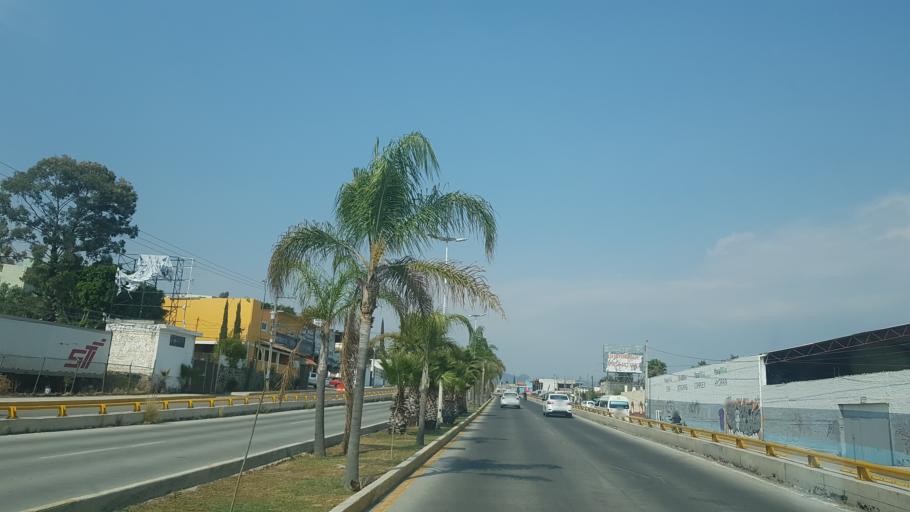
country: MX
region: Puebla
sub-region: Atlixco
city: El Encanto del Cerril
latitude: 18.9197
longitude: -98.4191
